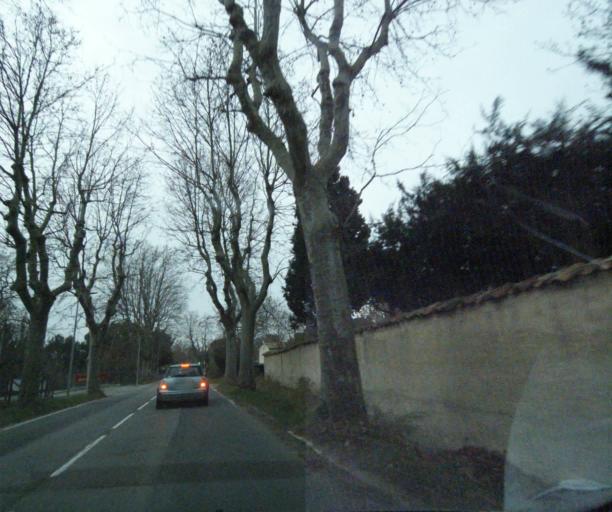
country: FR
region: Provence-Alpes-Cote d'Azur
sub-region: Departement des Bouches-du-Rhone
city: Aix-en-Provence
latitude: 43.5591
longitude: 5.4612
